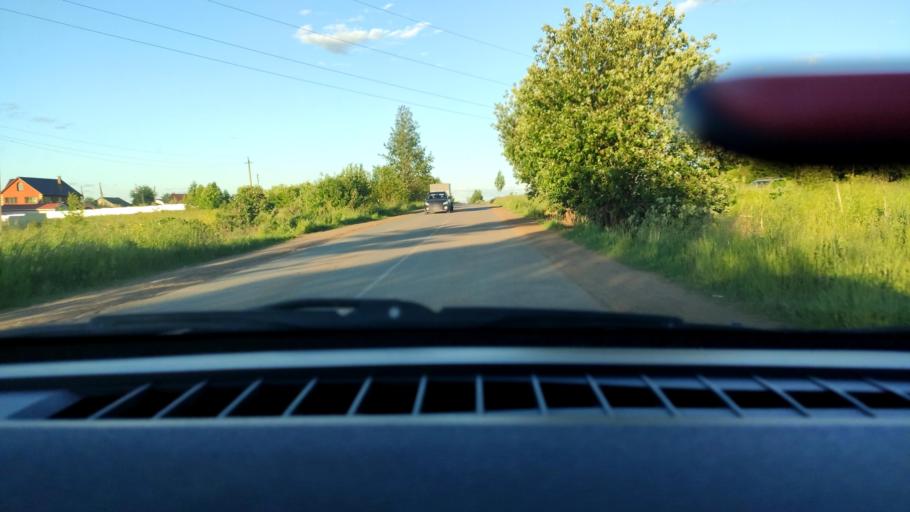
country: RU
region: Perm
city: Kultayevo
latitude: 57.9289
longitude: 55.8655
